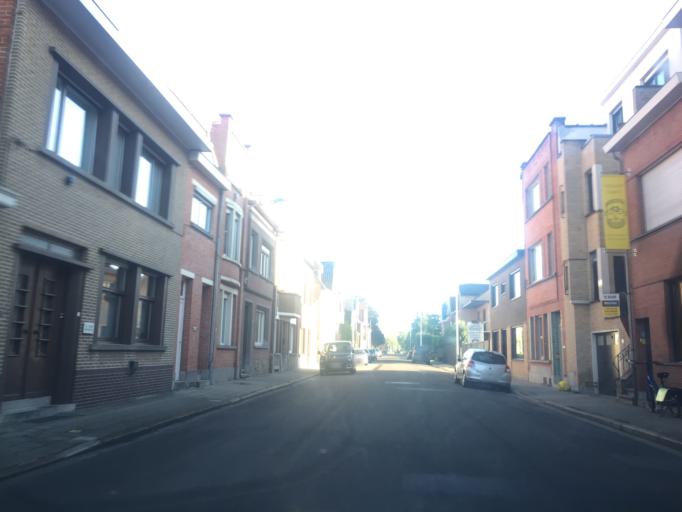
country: BE
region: Flanders
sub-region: Provincie West-Vlaanderen
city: Izegem
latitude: 50.9141
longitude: 3.2083
